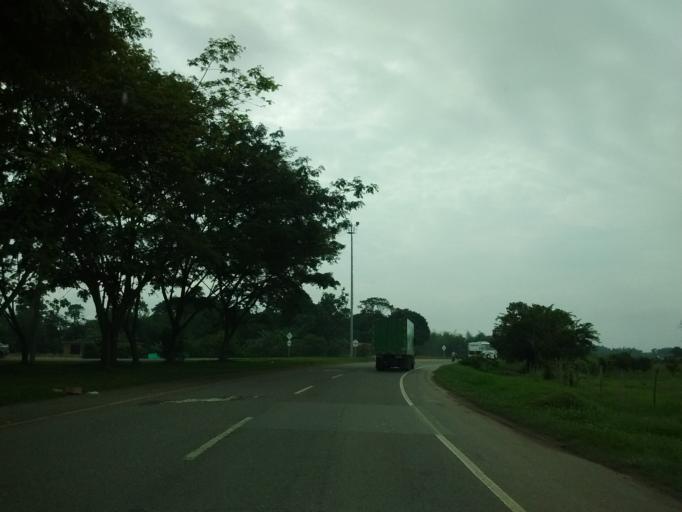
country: CO
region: Cauca
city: Puerto Tejada
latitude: 3.1856
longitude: -76.4481
